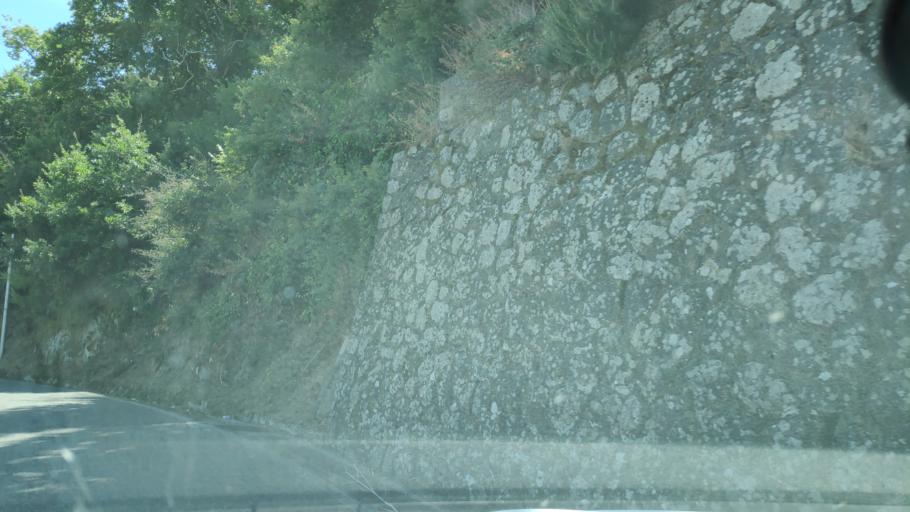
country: IT
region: Calabria
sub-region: Provincia di Catanzaro
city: Gasperina
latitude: 38.7384
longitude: 16.5105
